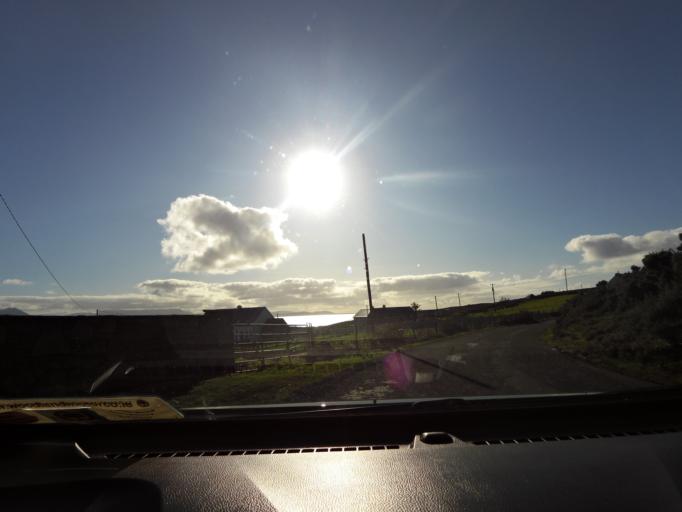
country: IE
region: Connaught
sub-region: Maigh Eo
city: Westport
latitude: 53.8824
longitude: -9.8112
